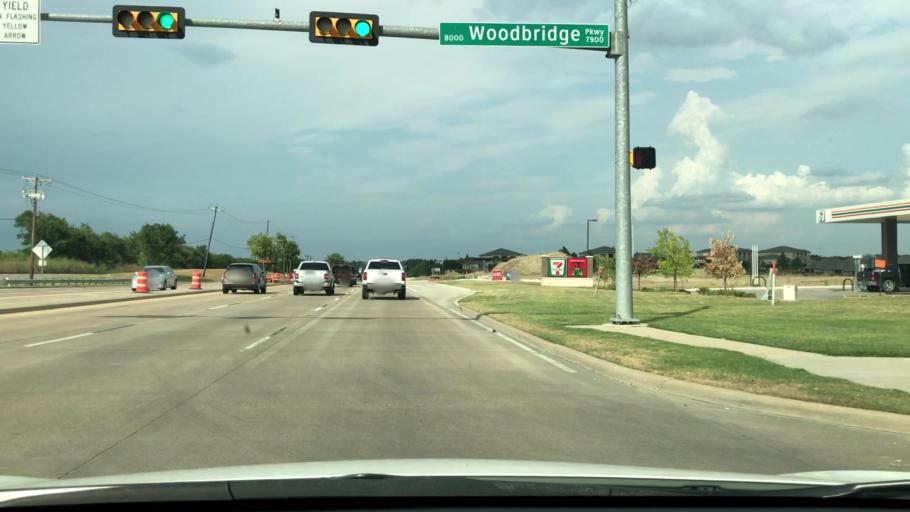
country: US
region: Texas
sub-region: Dallas County
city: Sachse
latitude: 32.9917
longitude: -96.5712
